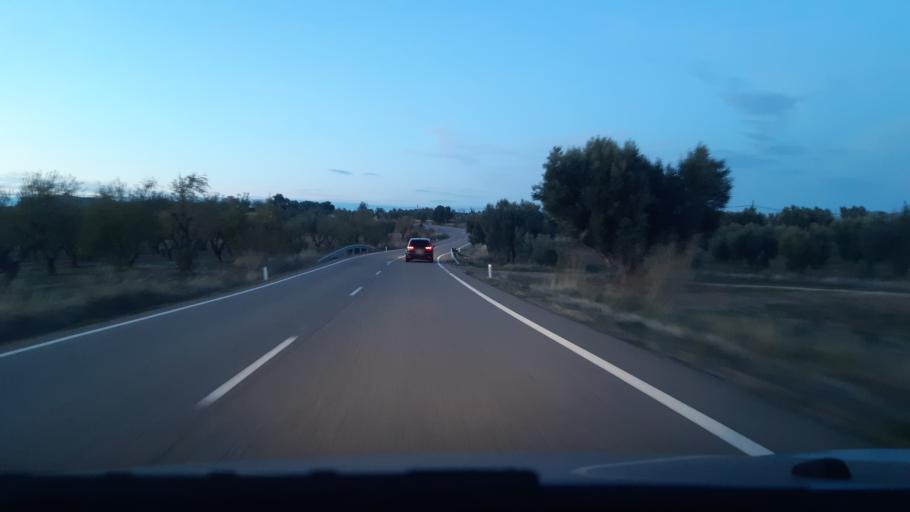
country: ES
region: Aragon
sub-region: Provincia de Teruel
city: Calaceite
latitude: 40.9883
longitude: 0.1992
